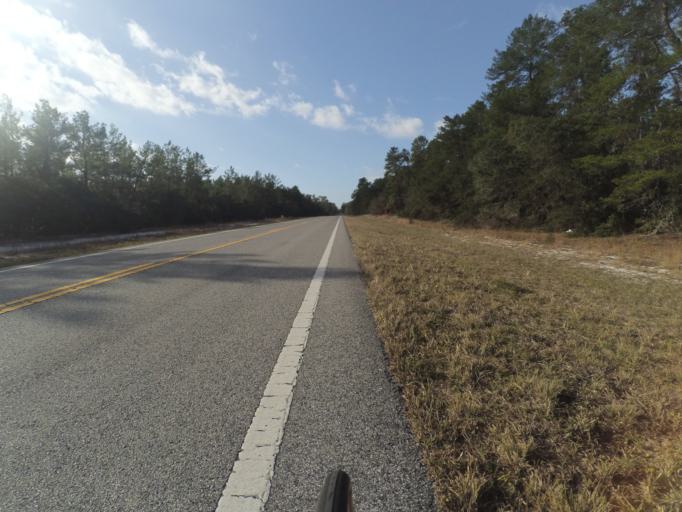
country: US
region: Florida
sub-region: Lake County
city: Astor
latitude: 29.1209
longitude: -81.6147
